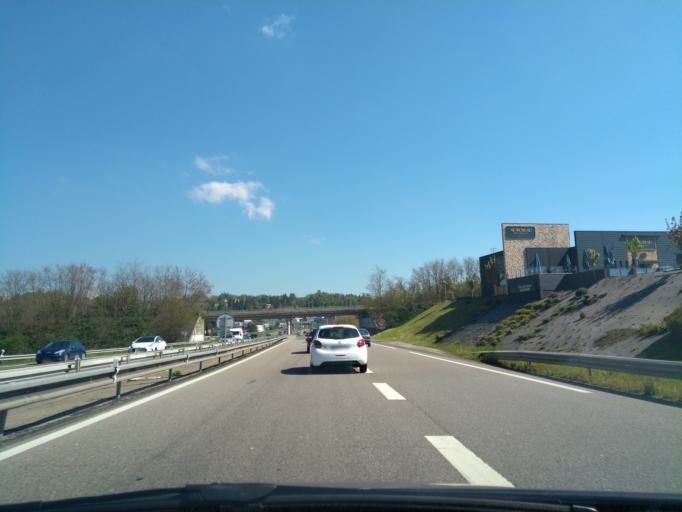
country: FR
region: Rhone-Alpes
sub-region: Departement de la Loire
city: Villars
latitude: 45.4771
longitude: 4.3466
